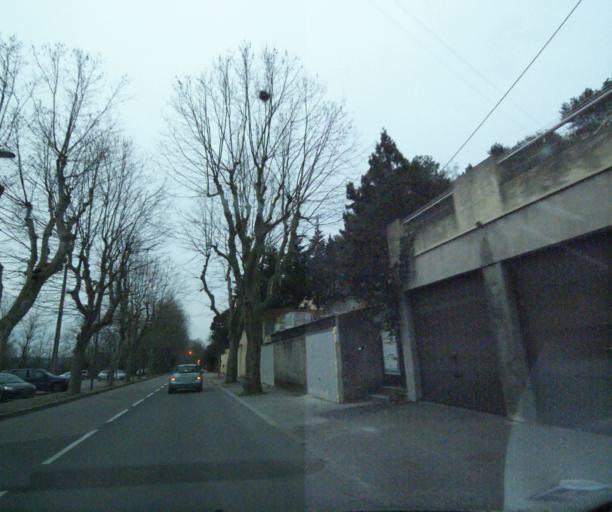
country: FR
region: Provence-Alpes-Cote d'Azur
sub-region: Departement des Bouches-du-Rhone
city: Aix-en-Provence
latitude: 43.5377
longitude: 5.4572
